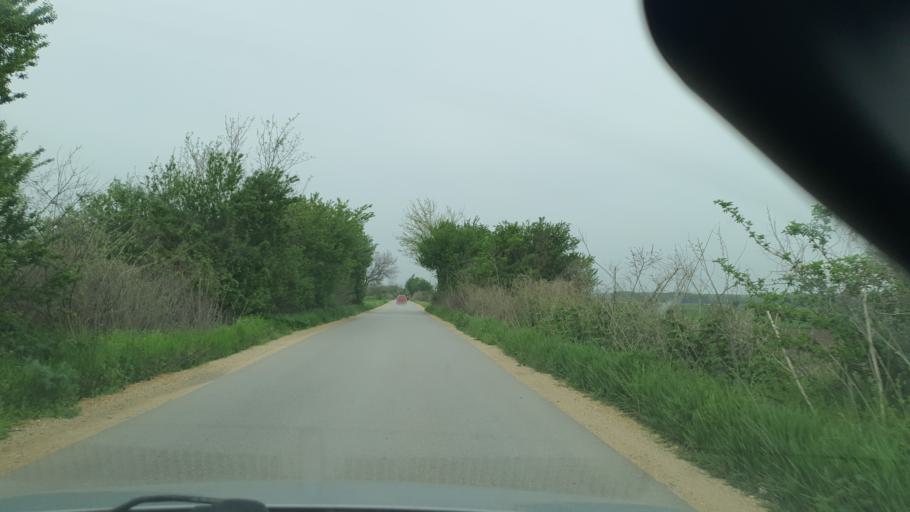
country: RS
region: Central Serbia
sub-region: Branicevski Okrug
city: Pozarevac
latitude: 44.7130
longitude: 21.1384
